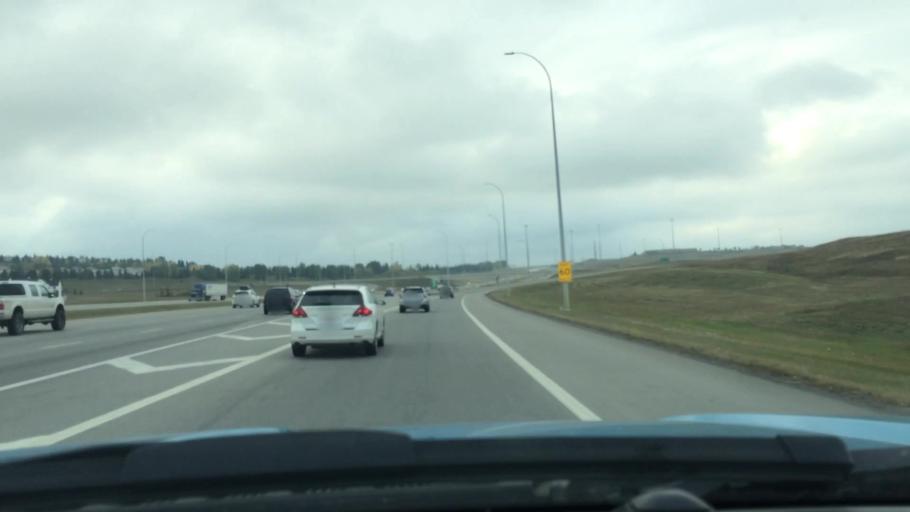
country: CA
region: Alberta
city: Calgary
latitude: 51.1534
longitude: -114.1292
